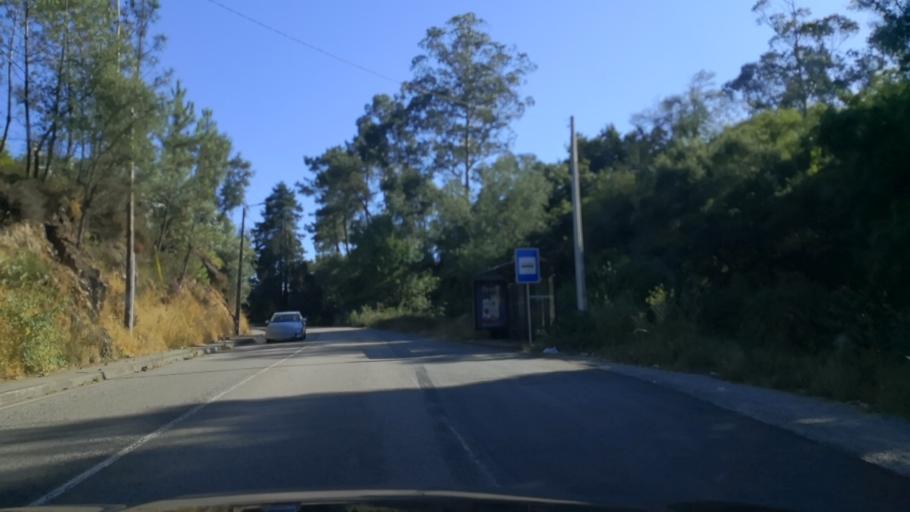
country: PT
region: Porto
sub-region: Santo Tirso
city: Sao Miguel do Couto
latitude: 41.3117
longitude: -8.4711
